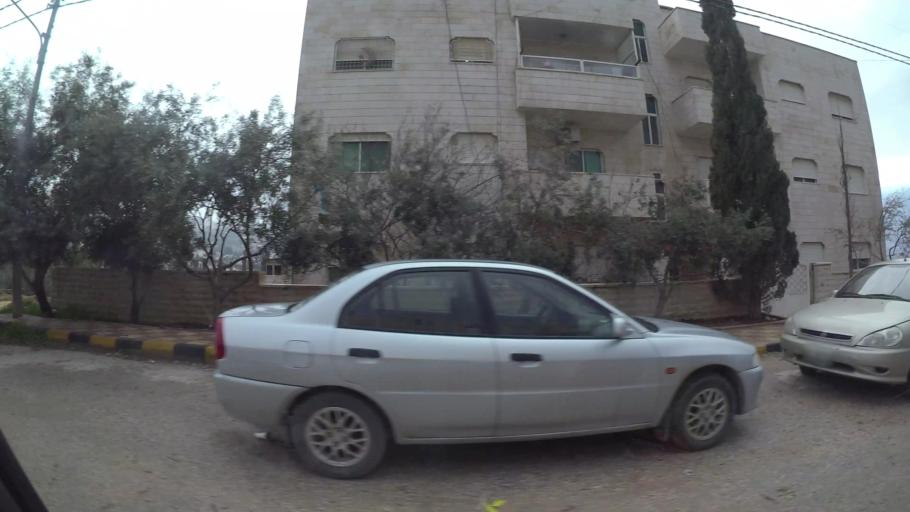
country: JO
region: Amman
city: Al Jubayhah
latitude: 32.0439
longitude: 35.8380
